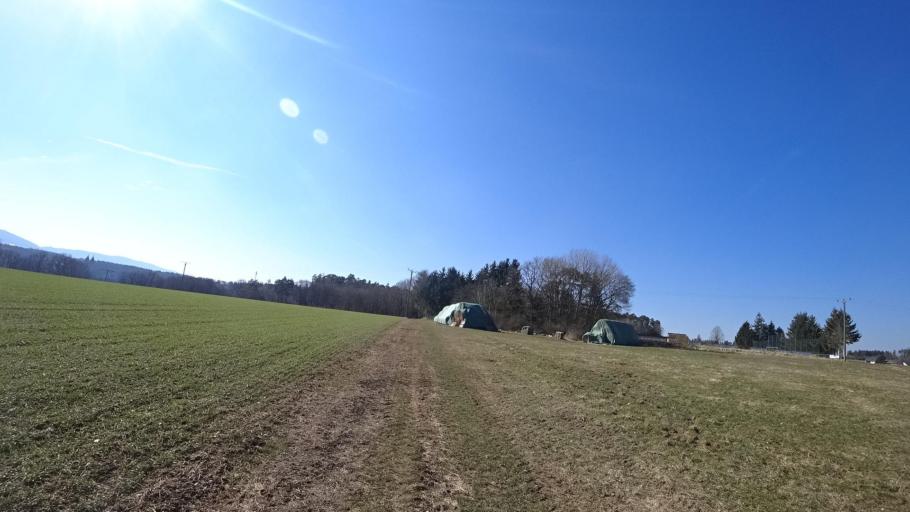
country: DE
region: Rheinland-Pfalz
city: Belgweiler
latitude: 49.9434
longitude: 7.4783
